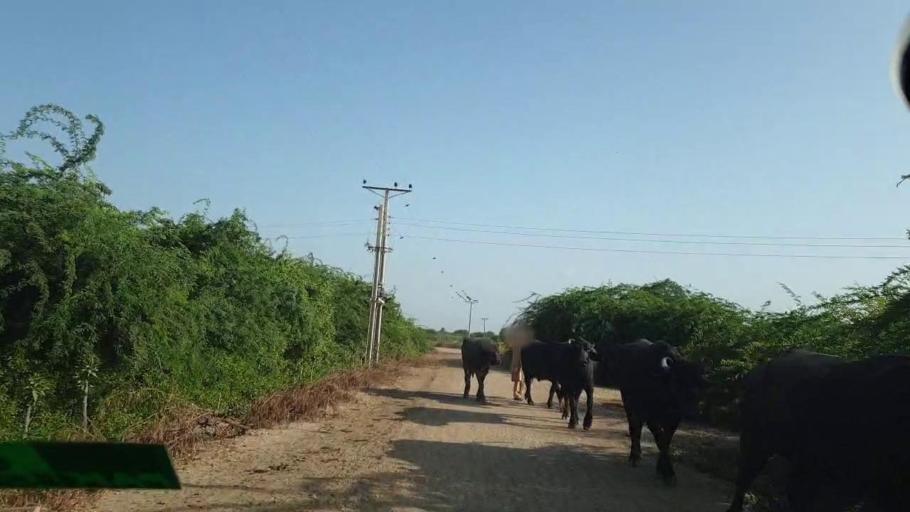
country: PK
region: Sindh
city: Naukot
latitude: 24.7339
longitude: 69.2506
